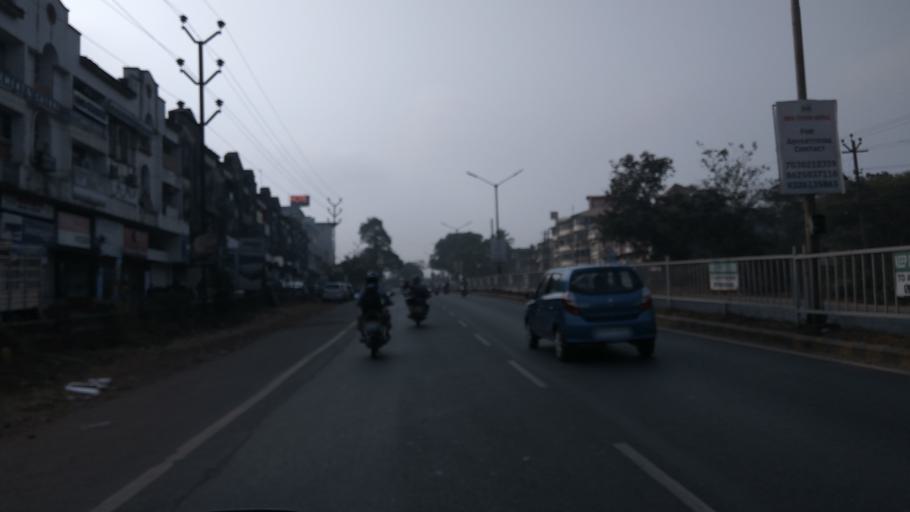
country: IN
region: Goa
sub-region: North Goa
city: Serula
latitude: 15.5281
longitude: 73.8260
